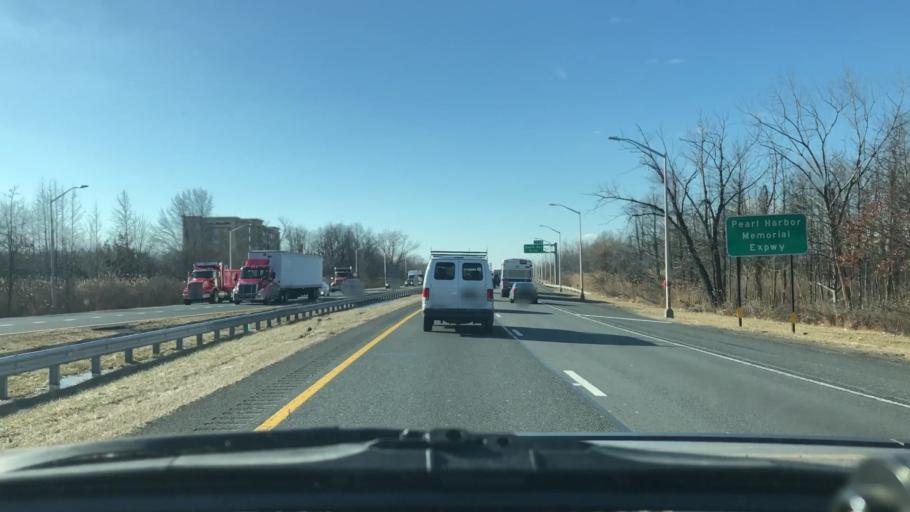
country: US
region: New York
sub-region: Richmond County
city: Bloomfield
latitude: 40.6157
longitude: -74.1784
